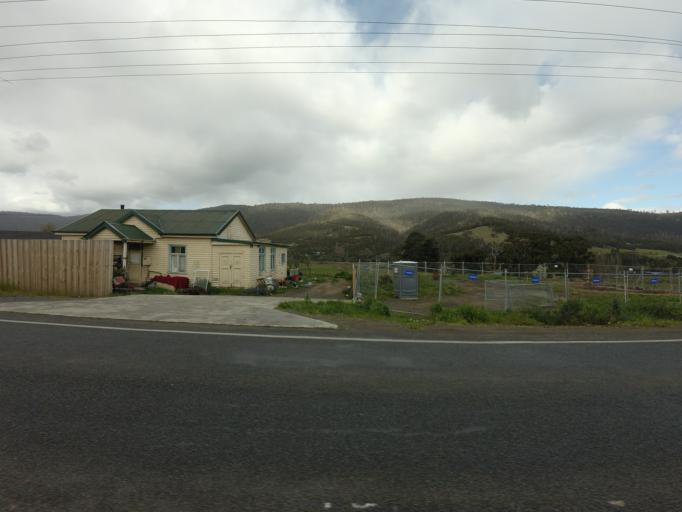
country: AU
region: Tasmania
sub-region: Huon Valley
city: Huonville
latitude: -43.0382
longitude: 147.0460
